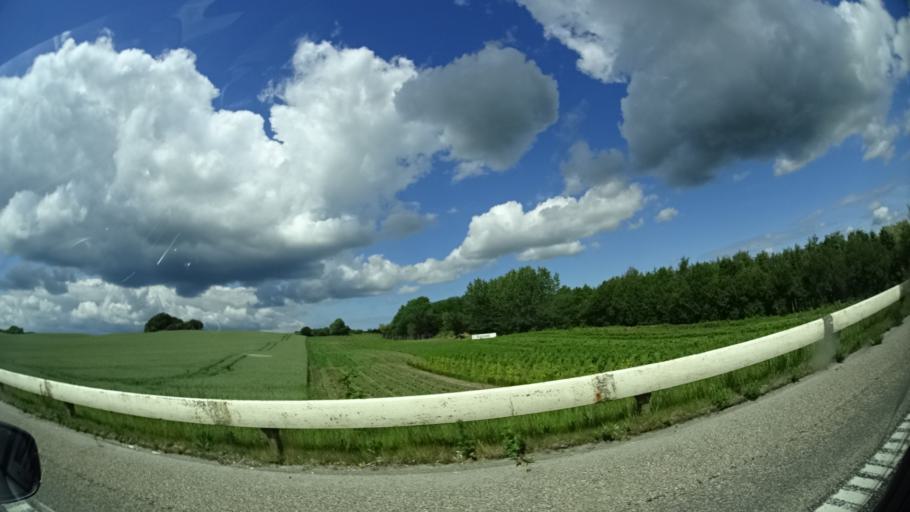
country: DK
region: Central Jutland
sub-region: Syddjurs Kommune
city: Ronde
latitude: 56.3172
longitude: 10.4793
